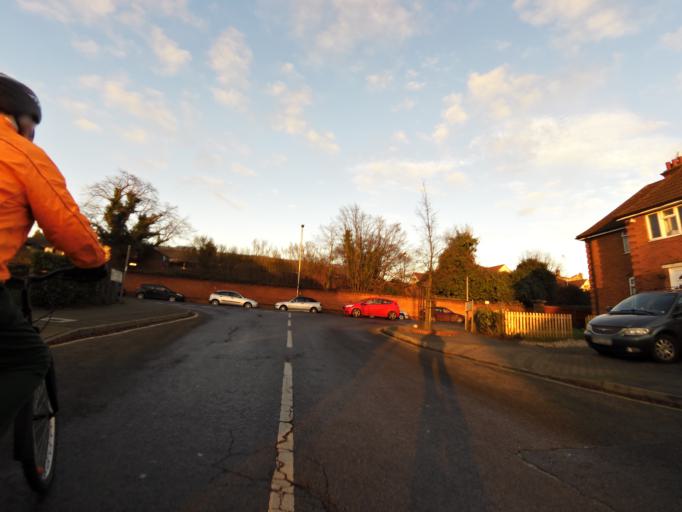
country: GB
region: England
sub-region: Suffolk
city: Ipswich
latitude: 52.0629
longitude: 1.1484
